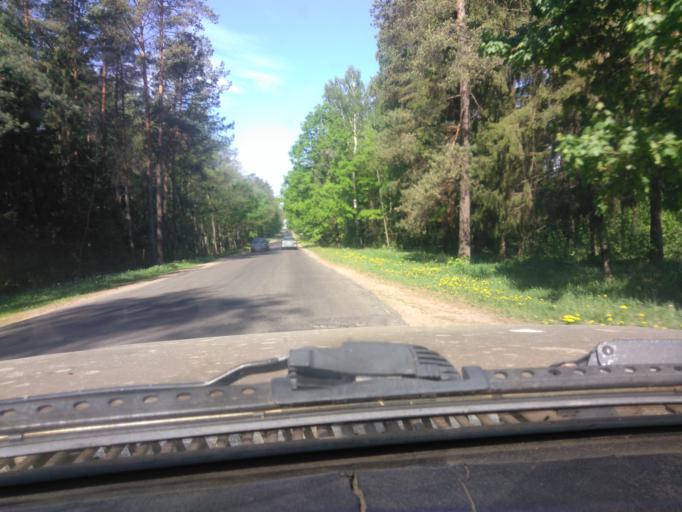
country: BY
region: Mogilev
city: Myazhysyatki
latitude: 53.8098
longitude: 30.1450
